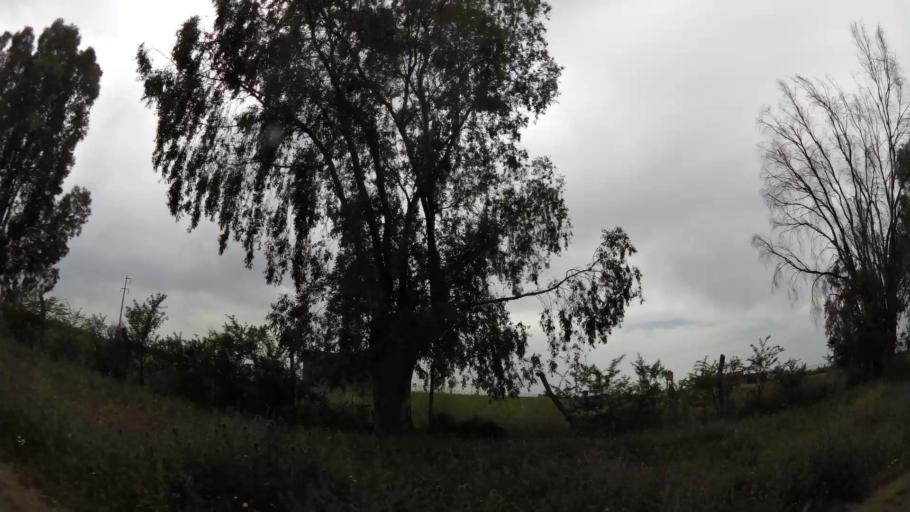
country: MA
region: Rabat-Sale-Zemmour-Zaer
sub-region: Khemisset
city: Tiflet
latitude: 33.8221
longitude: -6.2723
